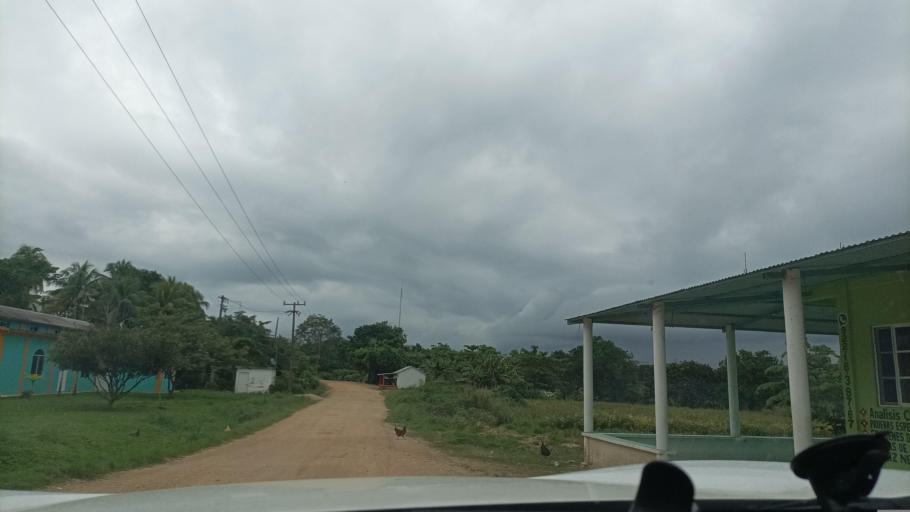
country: MX
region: Veracruz
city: Hidalgotitlan
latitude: 17.6402
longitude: -94.5119
